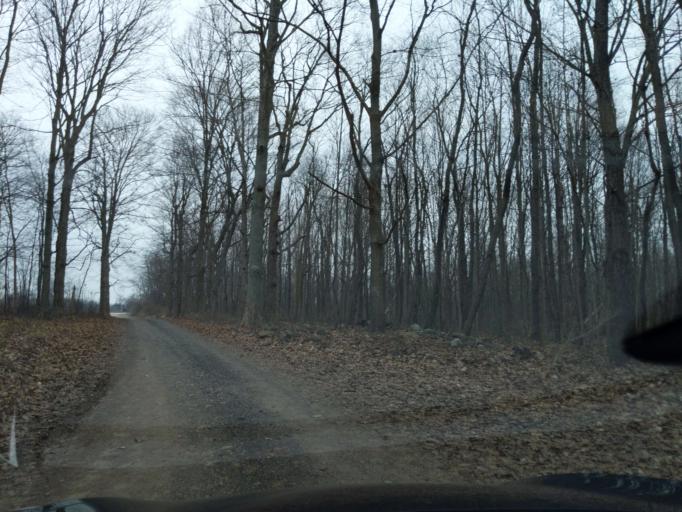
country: US
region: Michigan
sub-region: Eaton County
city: Potterville
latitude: 42.6185
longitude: -84.7563
